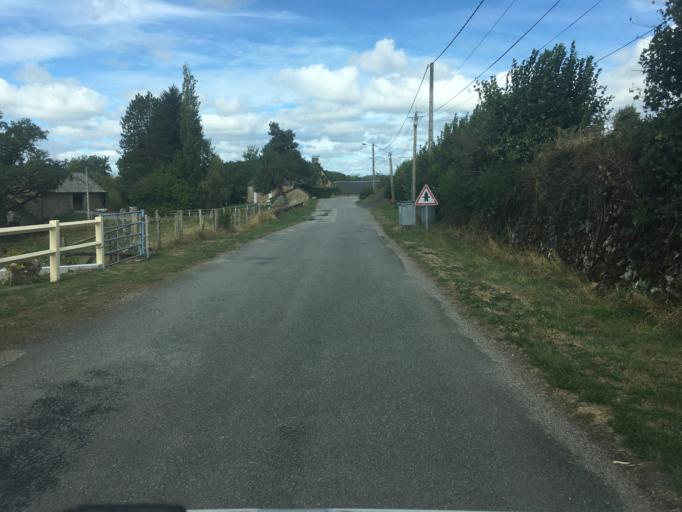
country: FR
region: Auvergne
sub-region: Departement du Cantal
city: Champagnac
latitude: 45.4310
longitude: 2.4127
